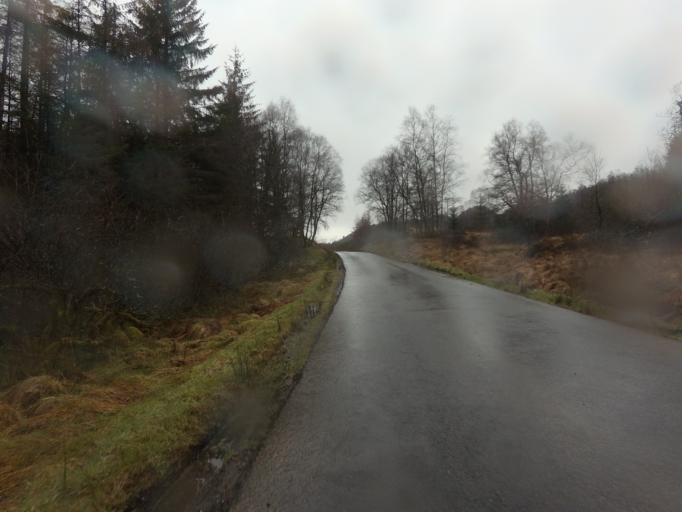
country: GB
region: Scotland
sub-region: West Dunbartonshire
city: Balloch
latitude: 56.2333
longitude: -4.5598
